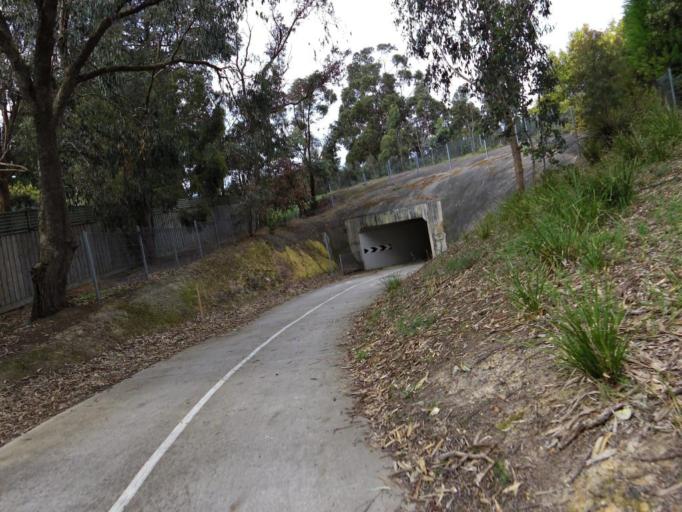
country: AU
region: Victoria
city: Mitcham
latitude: -37.7996
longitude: 145.1925
